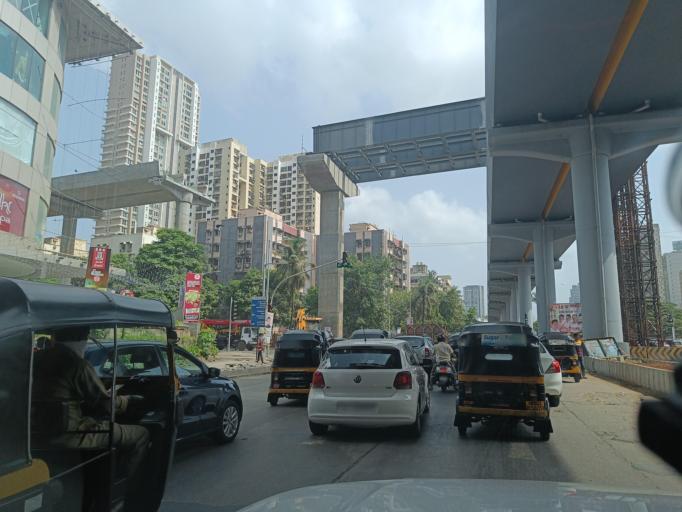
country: IN
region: Maharashtra
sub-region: Mumbai Suburban
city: Powai
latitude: 19.1408
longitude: 72.8314
